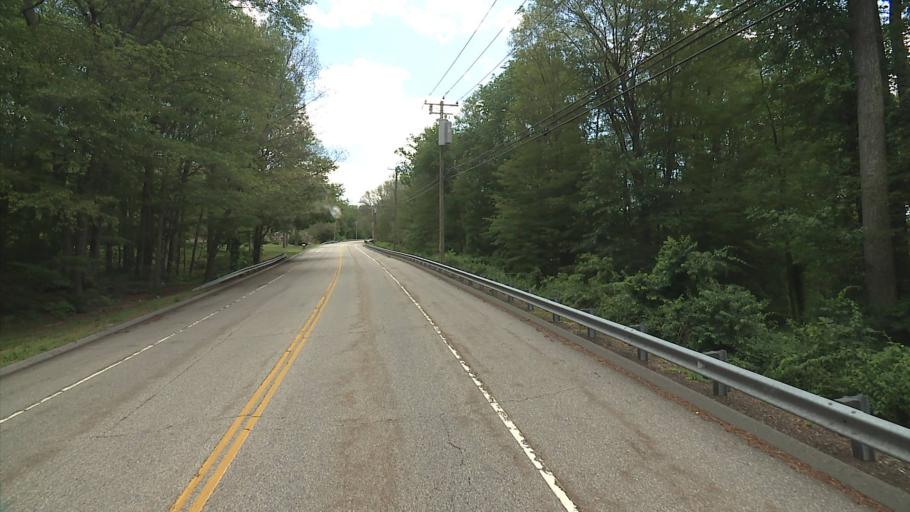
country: US
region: Connecticut
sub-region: Middlesex County
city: Higganum
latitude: 41.5265
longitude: -72.5303
